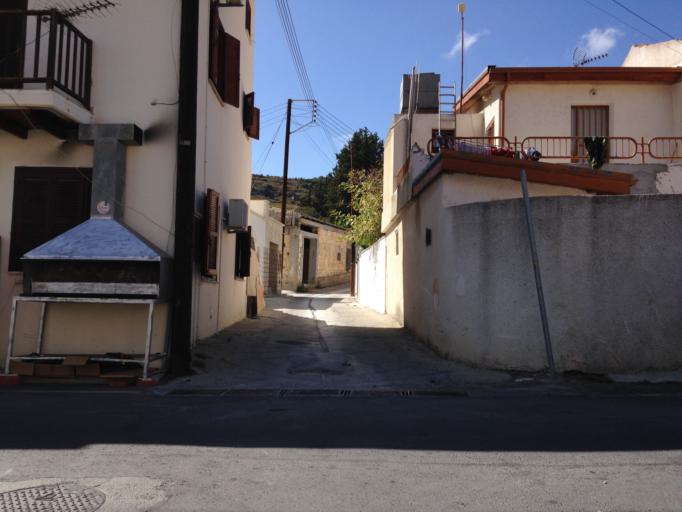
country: CY
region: Limassol
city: Pachna
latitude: 34.8490
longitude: 32.8080
